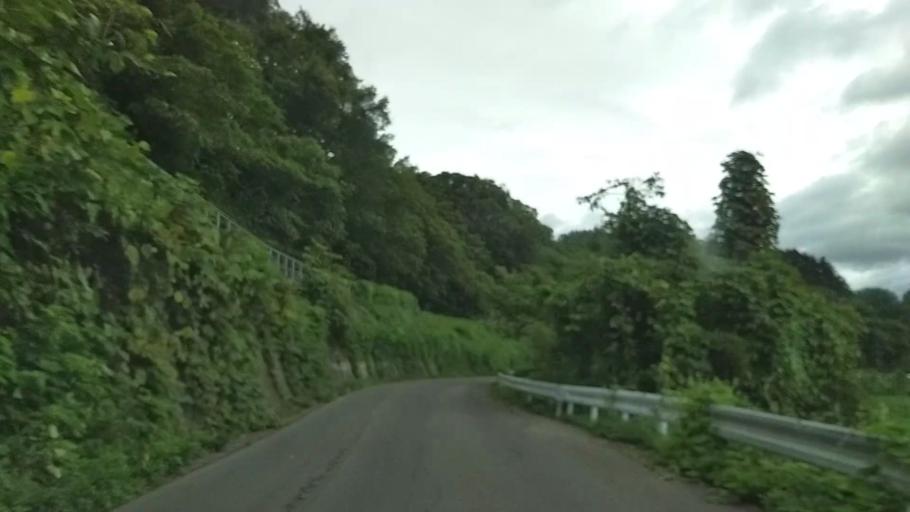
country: JP
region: Nagano
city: Iiyama
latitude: 36.8040
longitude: 138.3441
